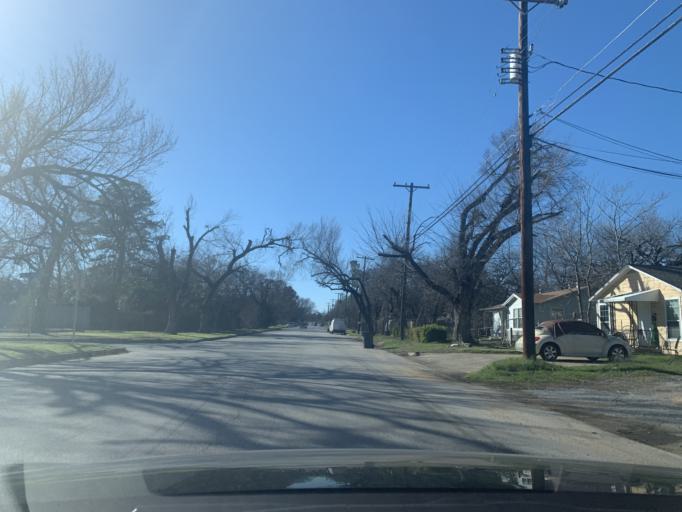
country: US
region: Texas
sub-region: Tarrant County
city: Haltom City
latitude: 32.7818
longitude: -97.2827
